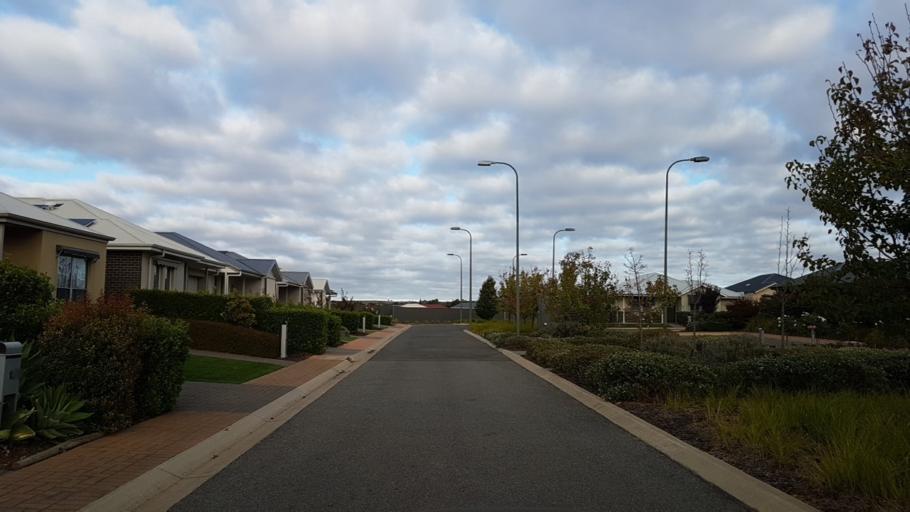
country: AU
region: South Australia
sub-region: Alexandrina
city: Strathalbyn
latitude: -35.2637
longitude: 138.8990
